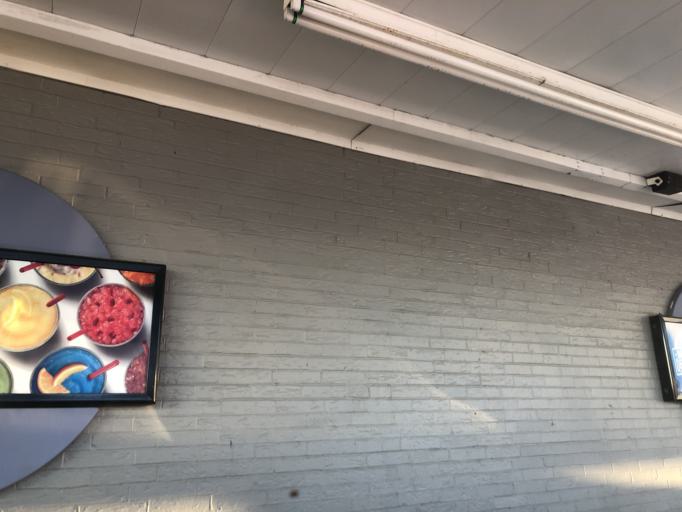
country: US
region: Texas
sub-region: Tarrant County
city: Euless
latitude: 32.8405
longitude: -97.0833
